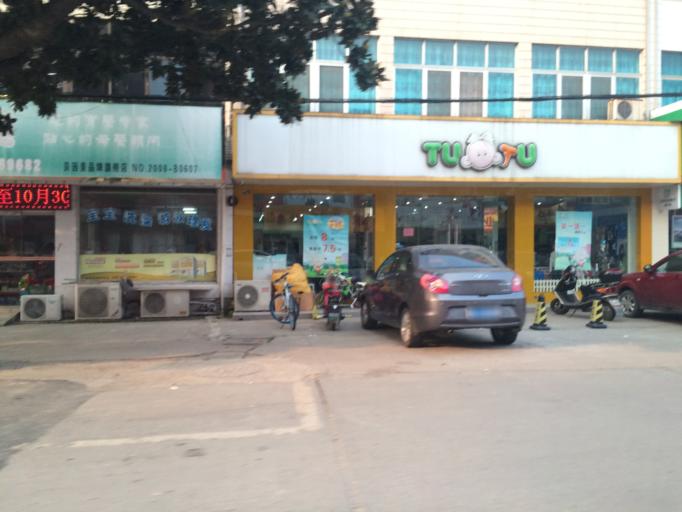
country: CN
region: Jiangsu Sheng
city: Xuxiake
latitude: 31.8125
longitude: 120.3007
